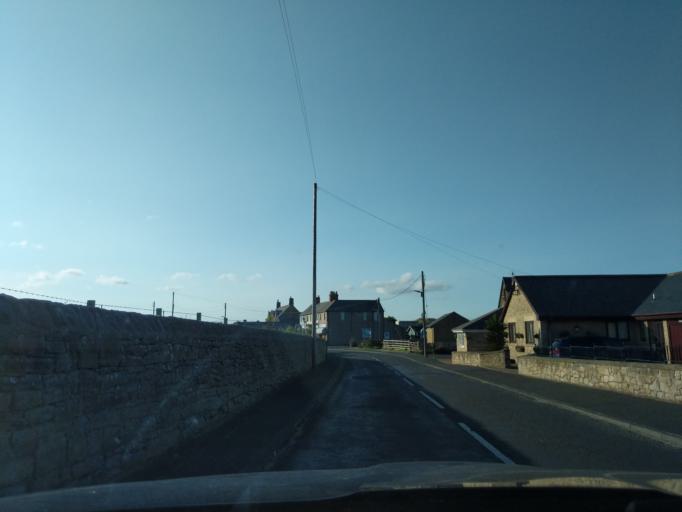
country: GB
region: England
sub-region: Northumberland
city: Cresswell
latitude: 55.2348
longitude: -1.5377
